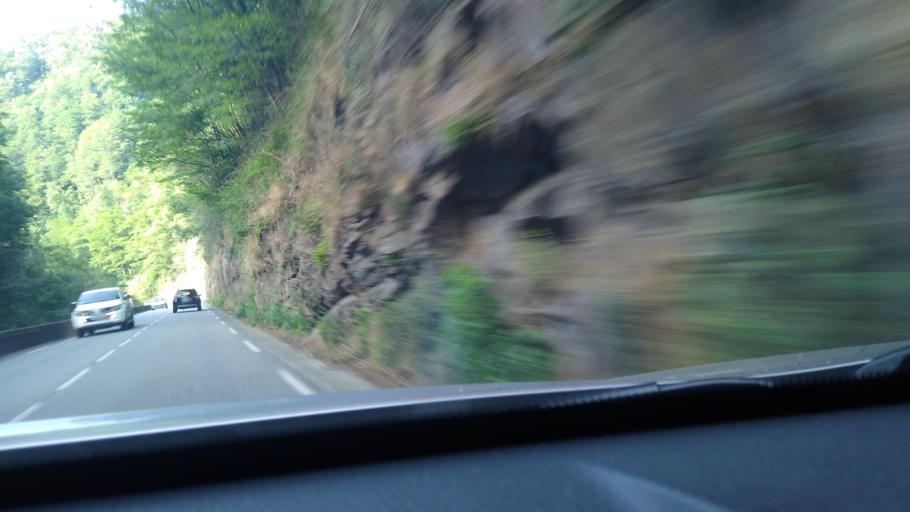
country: FR
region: Midi-Pyrenees
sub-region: Departement de l'Ariege
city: Saint-Girons
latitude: 42.9263
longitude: 1.1838
